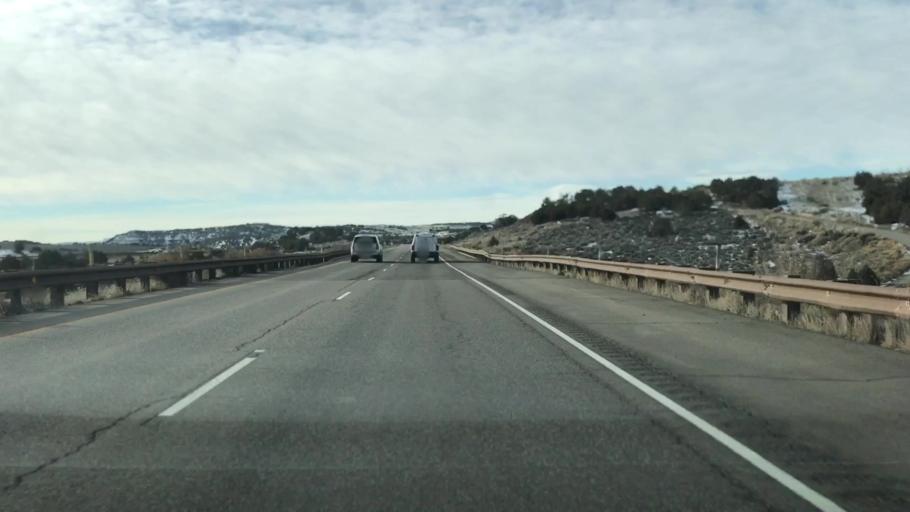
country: US
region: Colorado
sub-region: Garfield County
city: Parachute
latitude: 39.3761
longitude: -108.1618
